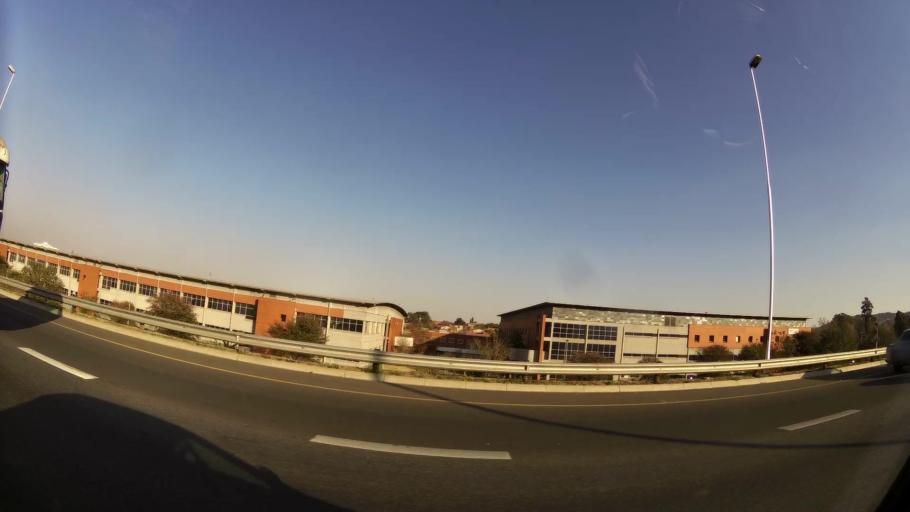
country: ZA
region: Gauteng
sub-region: Ekurhuleni Metropolitan Municipality
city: Germiston
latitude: -26.2594
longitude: 28.1133
